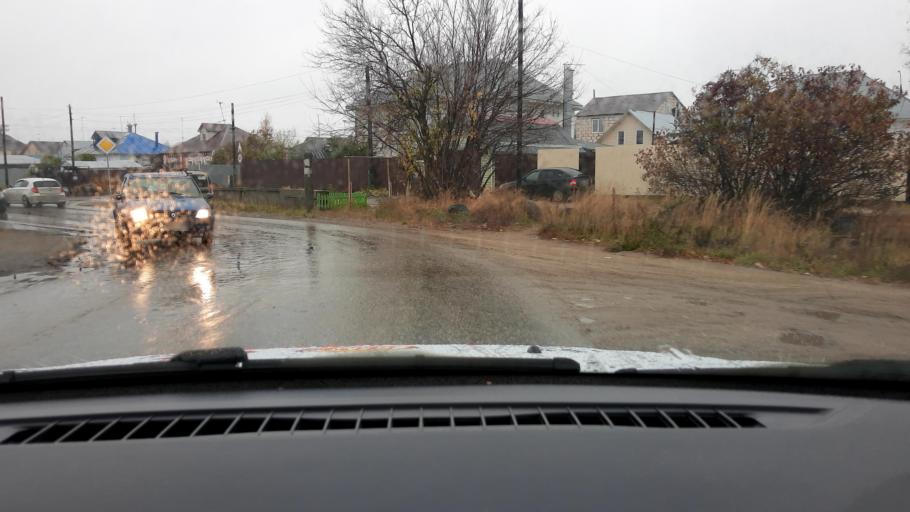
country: RU
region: Nizjnij Novgorod
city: Dzerzhinsk
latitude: 56.2413
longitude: 43.4080
